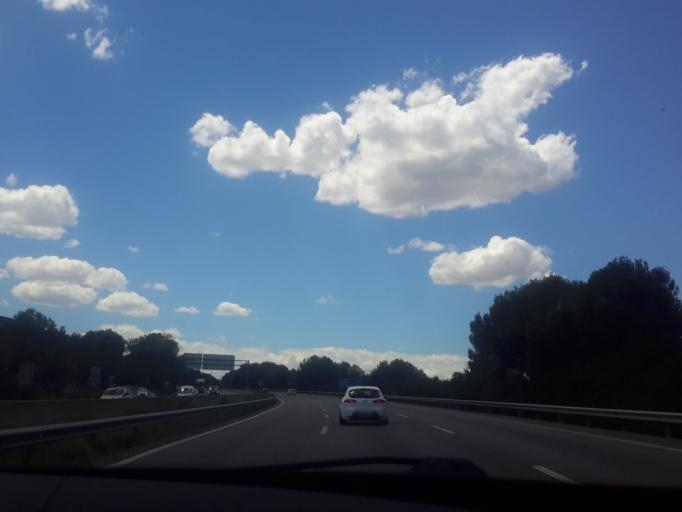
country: ES
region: Catalonia
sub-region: Provincia de Barcelona
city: Castellvi de Rosanes
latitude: 41.4586
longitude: 1.8909
